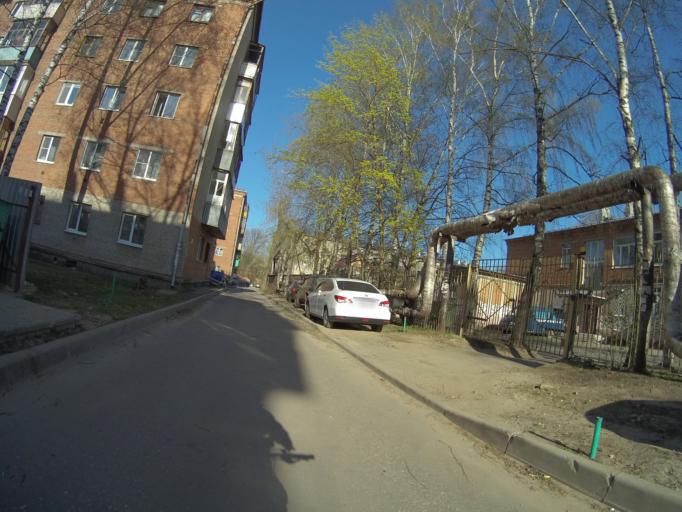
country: RU
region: Vladimir
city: Vladimir
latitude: 56.1496
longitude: 40.4164
